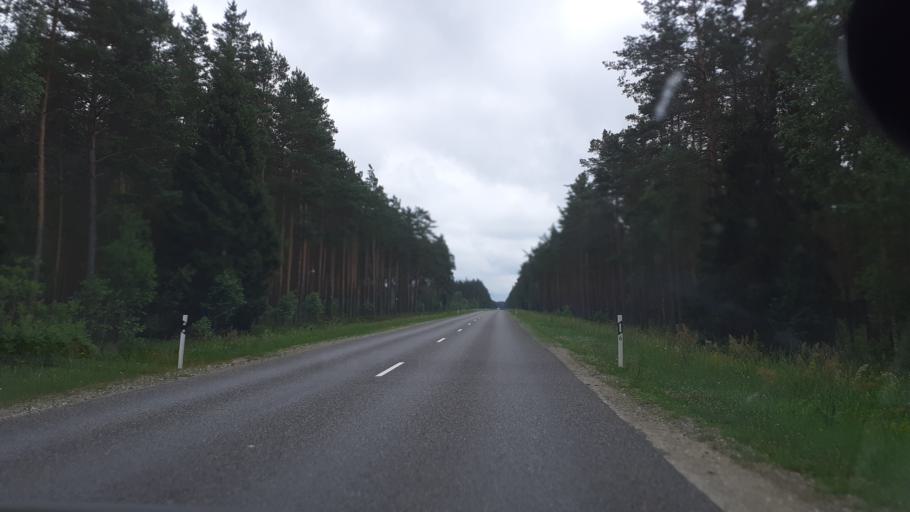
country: LV
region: Ventspils Rajons
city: Piltene
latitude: 57.1349
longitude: 21.7250
